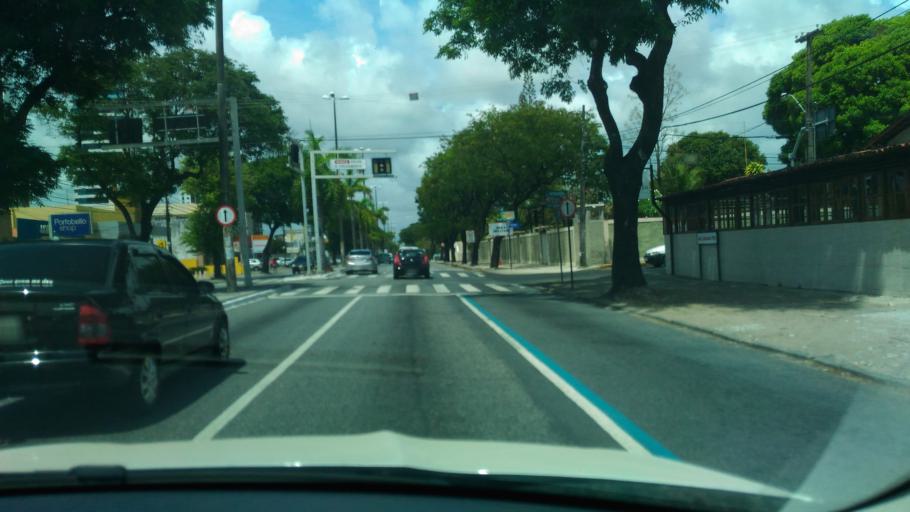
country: BR
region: Paraiba
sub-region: Joao Pessoa
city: Joao Pessoa
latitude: -7.1196
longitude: -34.8491
